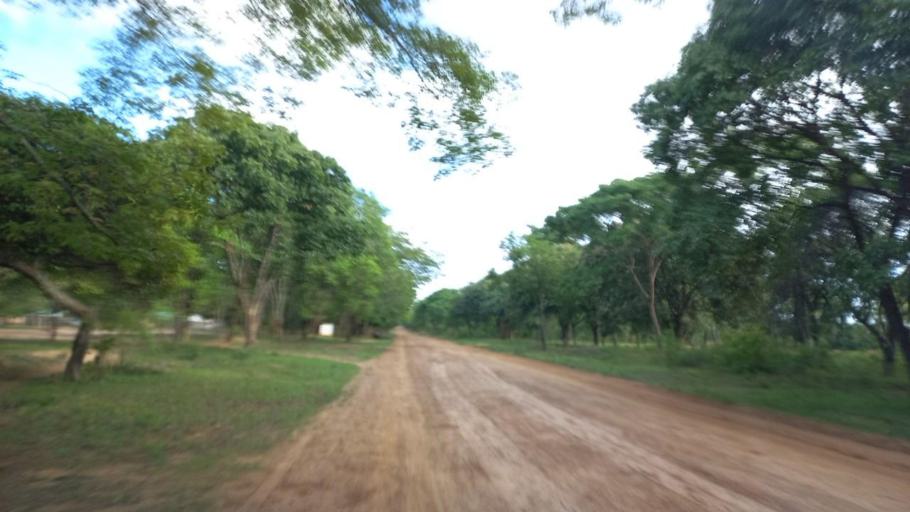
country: ZM
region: North-Western
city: Kabompo
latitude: -13.3699
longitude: 24.2967
